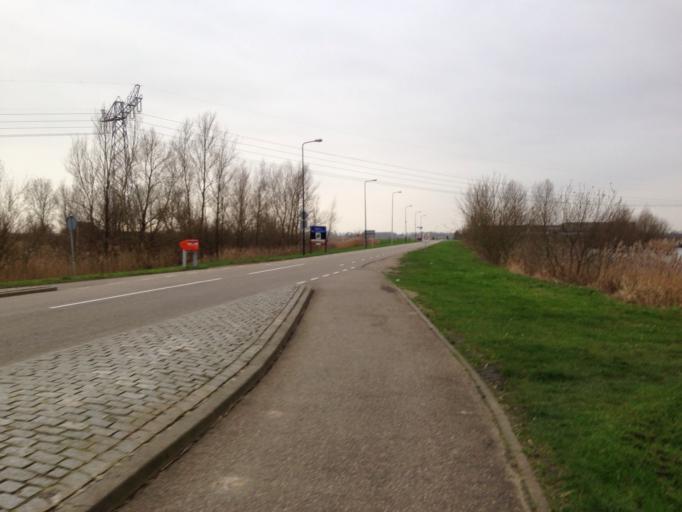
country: NL
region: Gelderland
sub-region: Gemeente Maasdriel
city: Hedel
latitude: 51.7216
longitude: 5.2460
